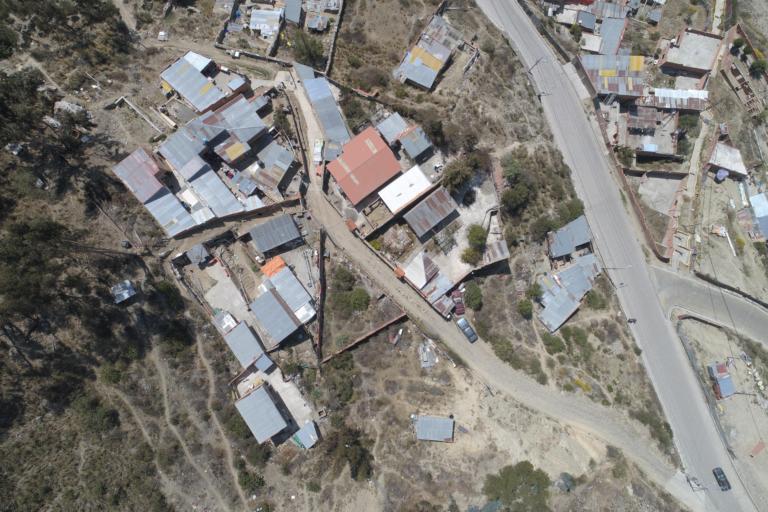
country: BO
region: La Paz
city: La Paz
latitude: -16.4983
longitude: -68.0997
